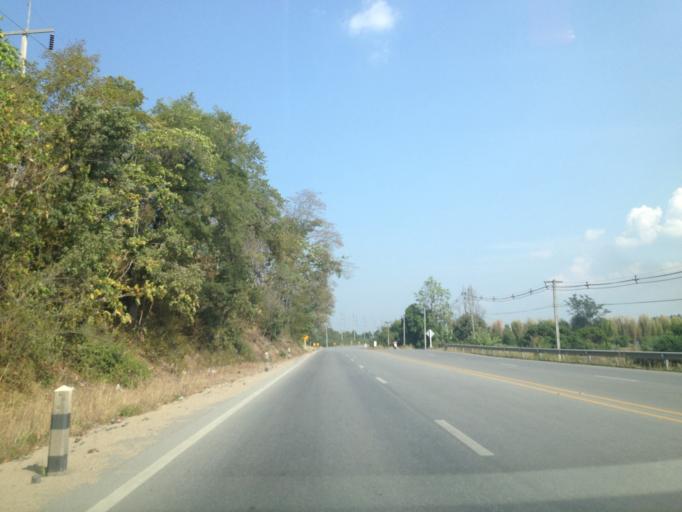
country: TH
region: Chiang Mai
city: Chom Thong
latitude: 18.3264
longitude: 98.6662
